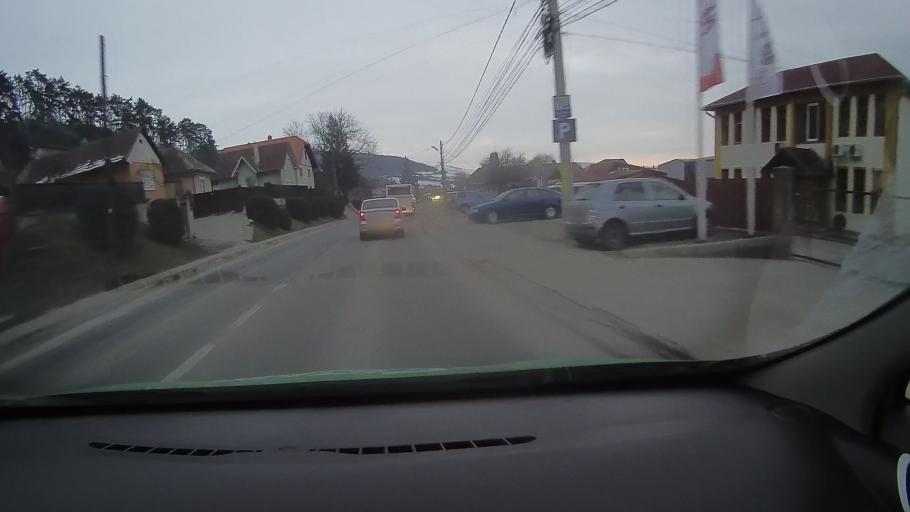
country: RO
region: Harghita
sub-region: Municipiul Odorheiu Secuiesc
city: Odorheiu Secuiesc
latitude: 46.2910
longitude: 25.2900
